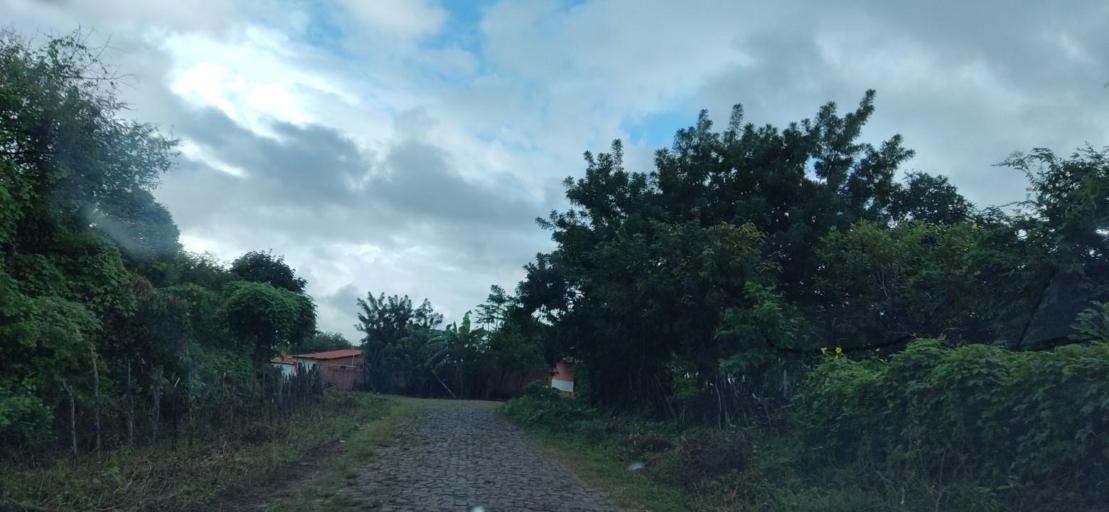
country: BR
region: Piaui
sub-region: Valenca Do Piaui
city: Valenca do Piaui
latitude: -6.1131
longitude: -41.7858
